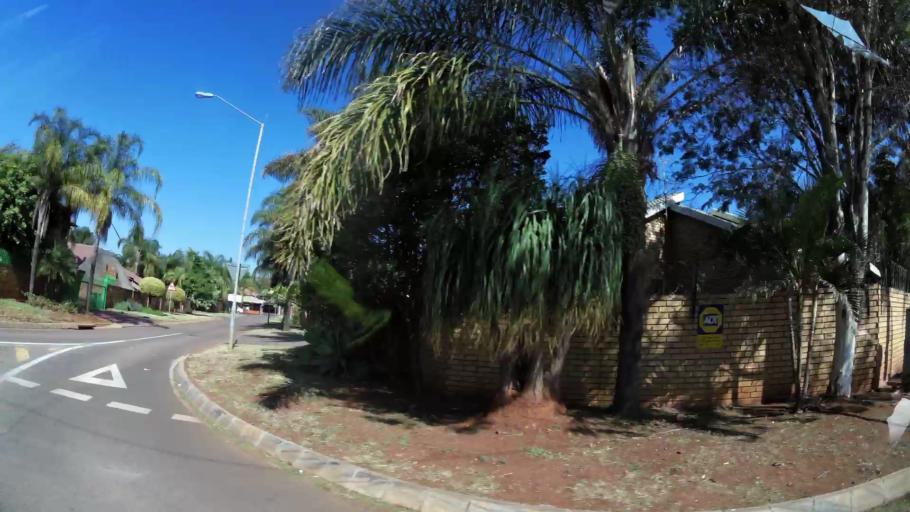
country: ZA
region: Gauteng
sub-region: City of Tshwane Metropolitan Municipality
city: Pretoria
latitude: -25.6850
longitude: 28.2751
